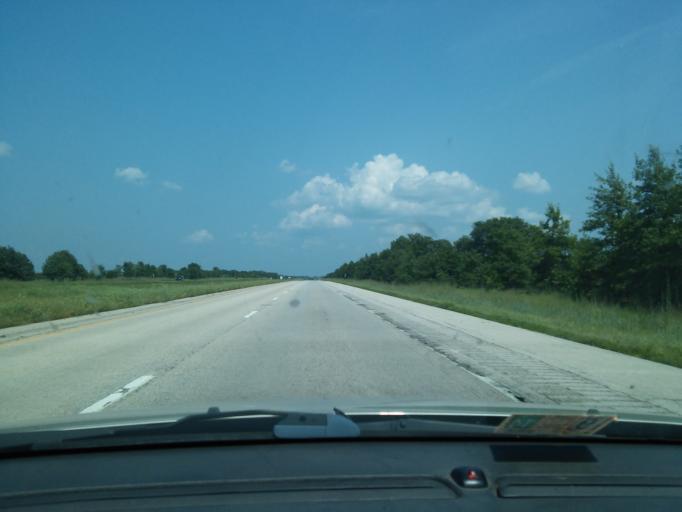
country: US
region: Illinois
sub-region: Sangamon County
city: New Berlin
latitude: 39.7448
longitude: -89.8161
